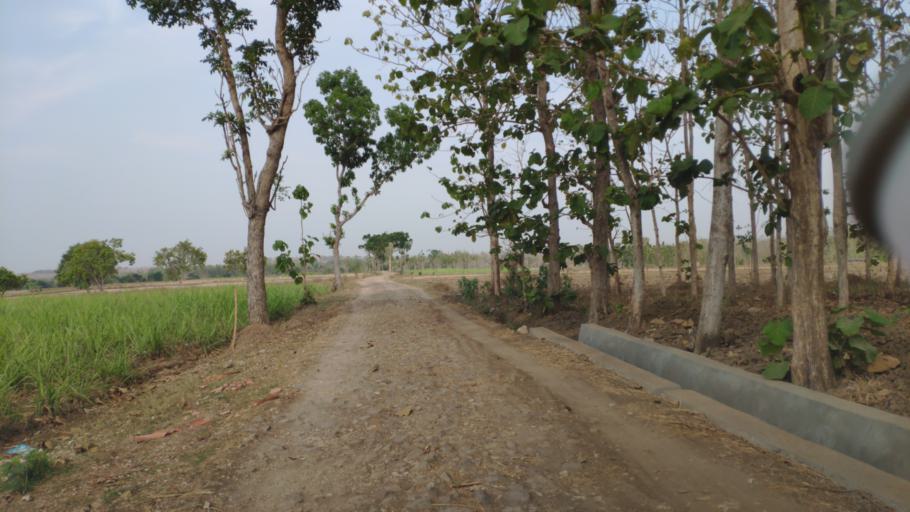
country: ID
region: Central Java
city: Triteh
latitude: -6.9632
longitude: 111.3543
